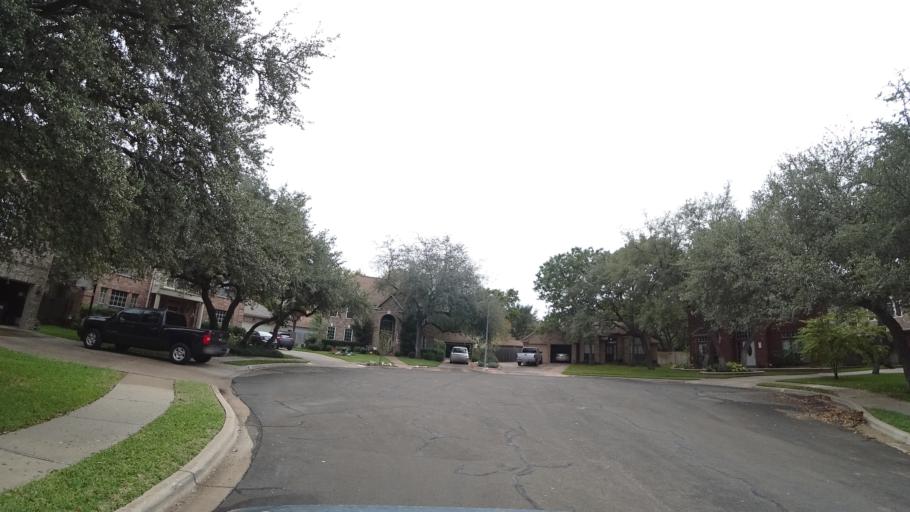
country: US
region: Texas
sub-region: Williamson County
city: Brushy Creek
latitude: 30.5189
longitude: -97.7129
